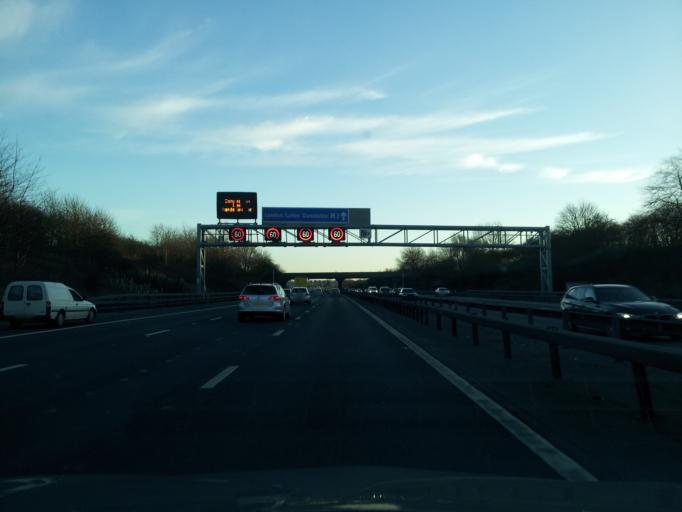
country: GB
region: England
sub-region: Central Bedfordshire
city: Toddington
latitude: 51.9763
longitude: -0.5261
